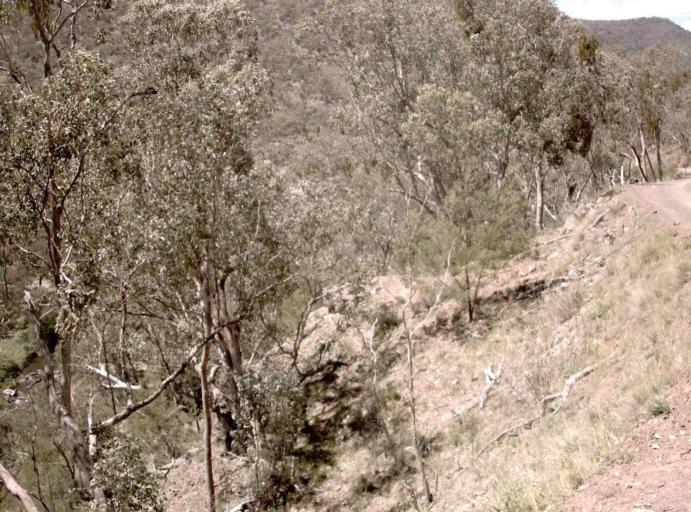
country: AU
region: New South Wales
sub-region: Snowy River
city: Jindabyne
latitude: -37.0795
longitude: 148.4523
